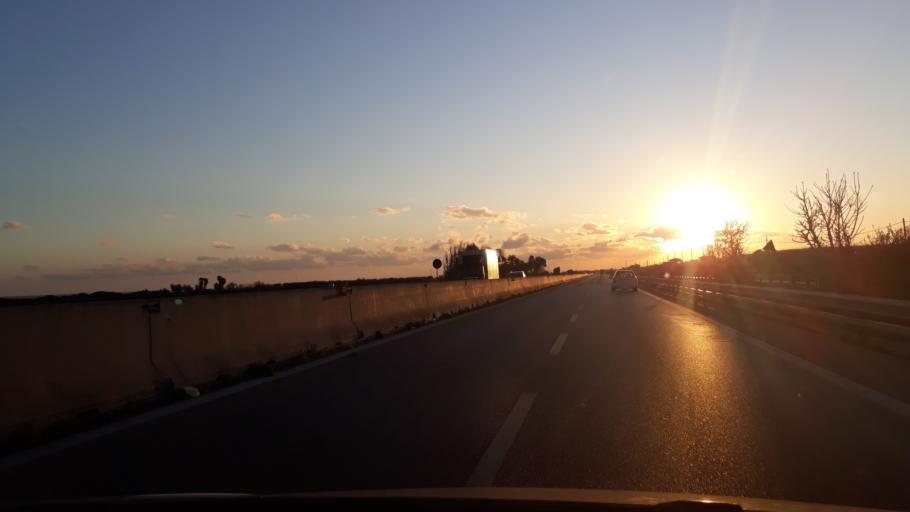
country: IT
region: Apulia
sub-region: Provincia di Brindisi
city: Montalbano
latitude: 40.8172
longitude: 17.5013
